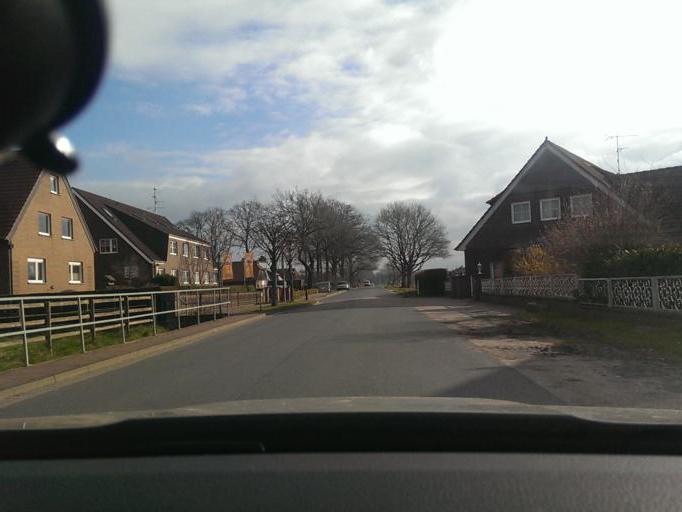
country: DE
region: Lower Saxony
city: Lindwedel
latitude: 52.5687
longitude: 9.6189
